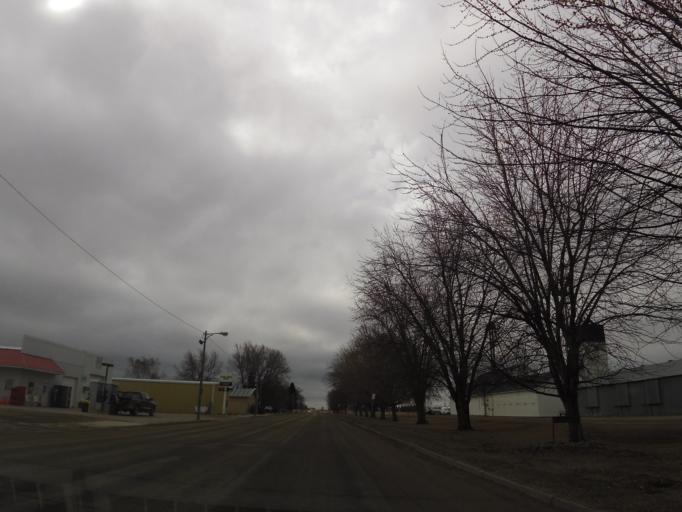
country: US
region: North Dakota
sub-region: Cass County
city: Casselton
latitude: 47.1024
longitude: -97.2182
